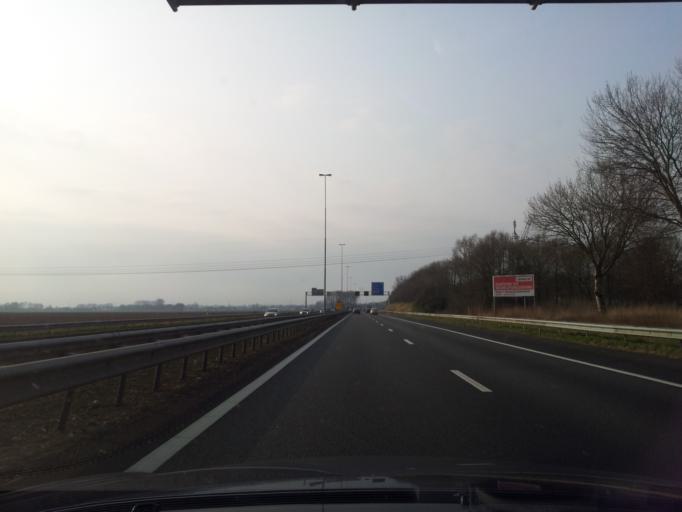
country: NL
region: North Brabant
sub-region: Gemeente Geertruidenberg
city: Geertruidenberg
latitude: 51.7064
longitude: 4.8885
